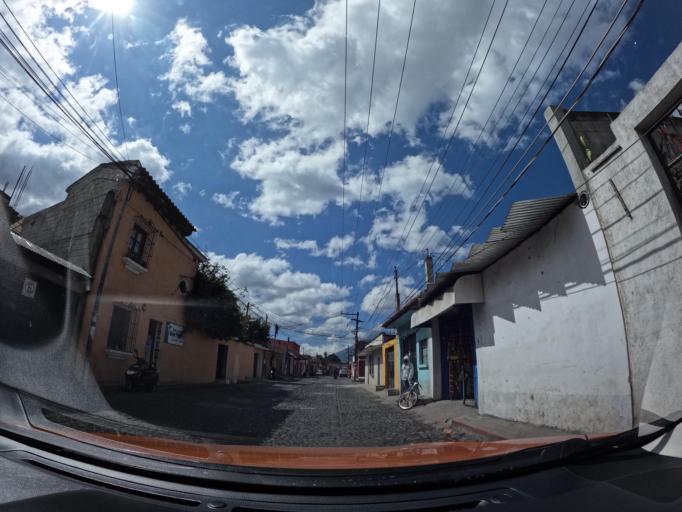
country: GT
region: Sacatepequez
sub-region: Municipio de Santa Maria de Jesus
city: Santa Maria de Jesus
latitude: 14.5327
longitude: -90.7364
